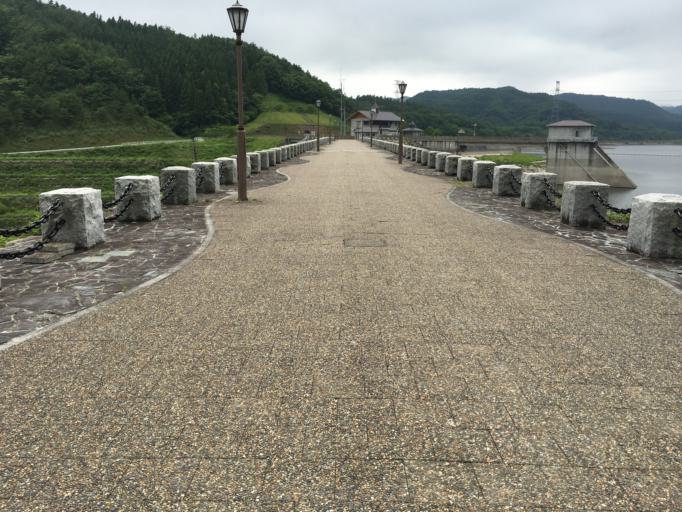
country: JP
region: Miyagi
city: Marumori
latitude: 37.7978
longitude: 140.7730
